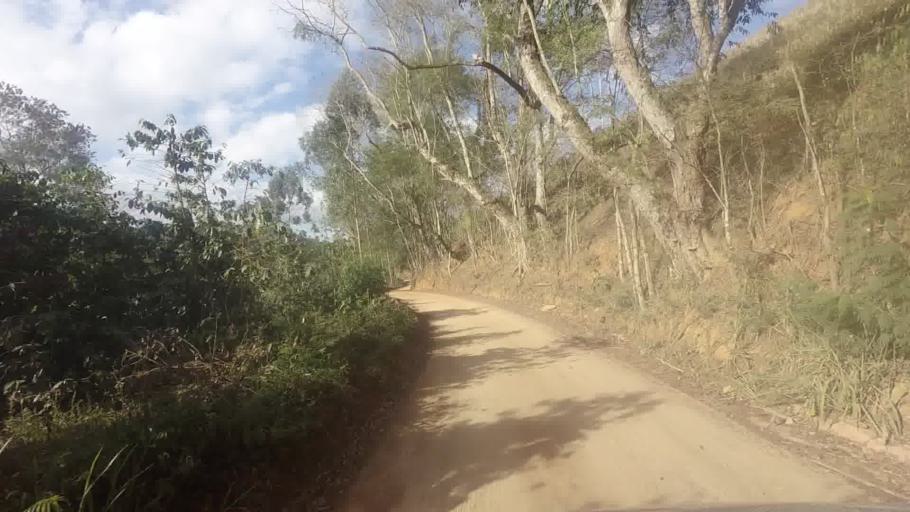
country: BR
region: Espirito Santo
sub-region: Sao Jose Do Calcado
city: Sao Jose do Calcado
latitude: -20.9792
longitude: -41.5132
